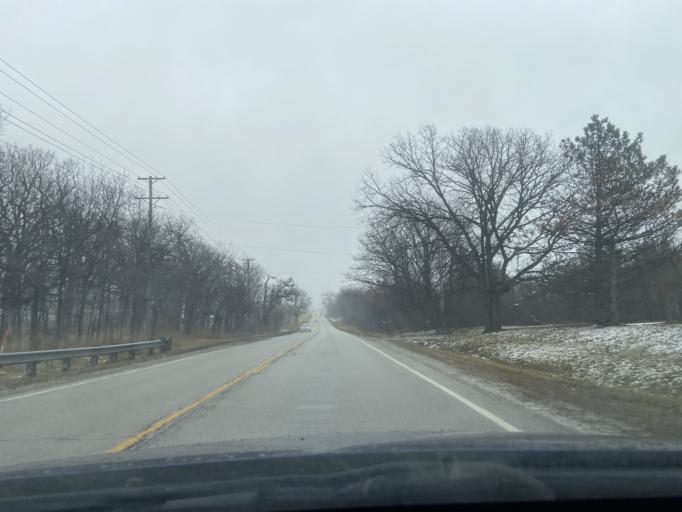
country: US
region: Illinois
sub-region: Lake County
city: Volo
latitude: 42.3191
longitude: -88.1331
